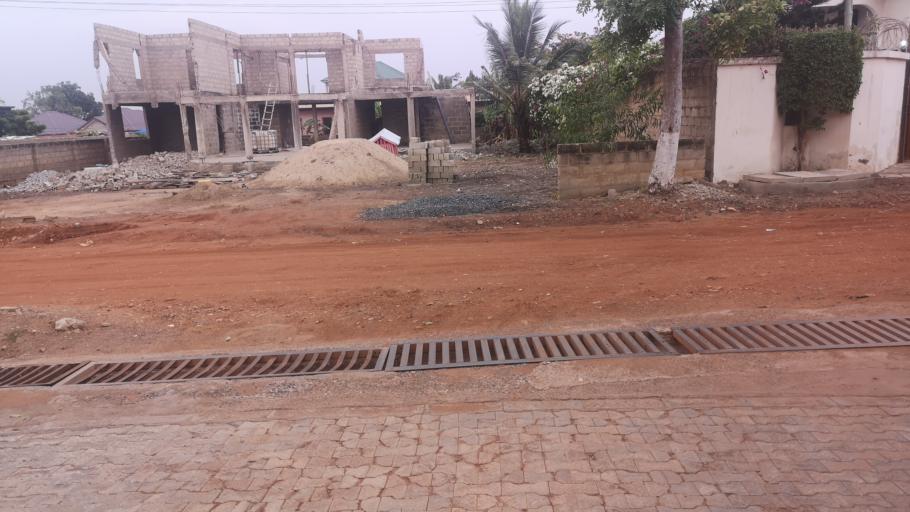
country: GH
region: Greater Accra
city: Nungua
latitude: 5.6376
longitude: -0.0787
